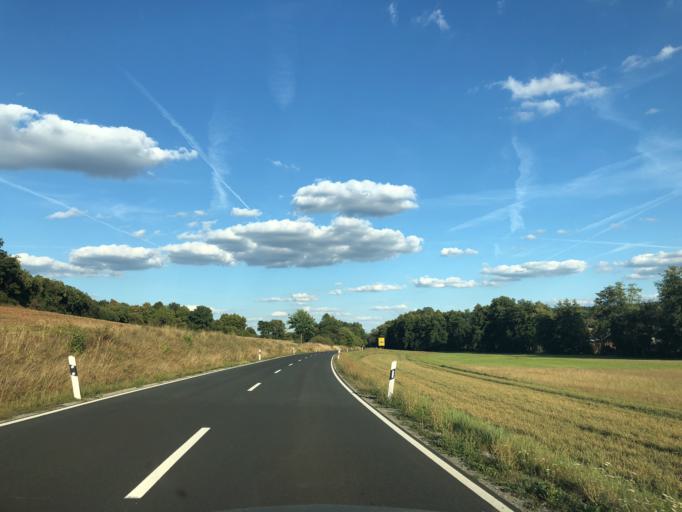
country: DE
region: Bavaria
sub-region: Upper Franconia
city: Burgwindheim
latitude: 49.8320
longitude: 10.5619
